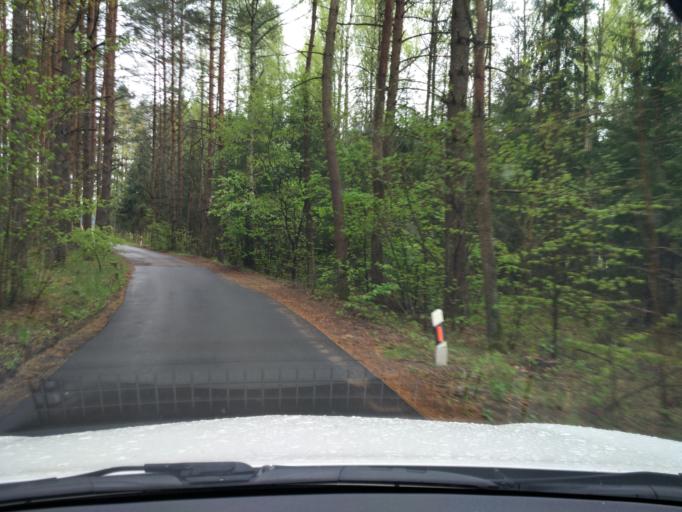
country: LT
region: Vilnius County
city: Rasos
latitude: 54.7402
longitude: 25.3983
